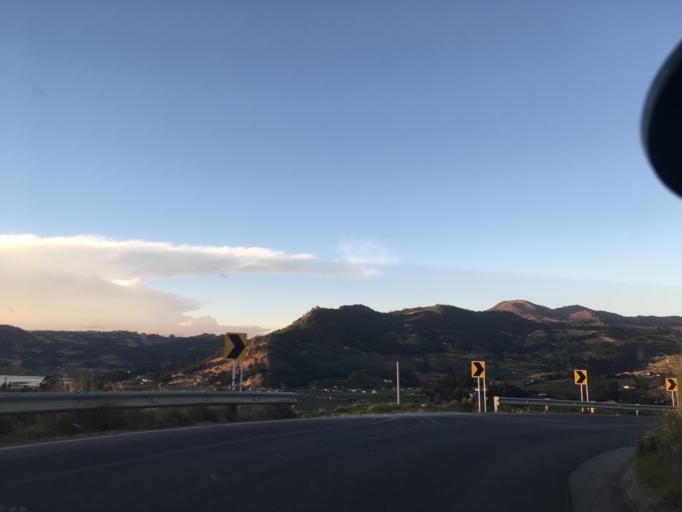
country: CO
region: Boyaca
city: Aquitania
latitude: 5.5732
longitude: -72.8951
